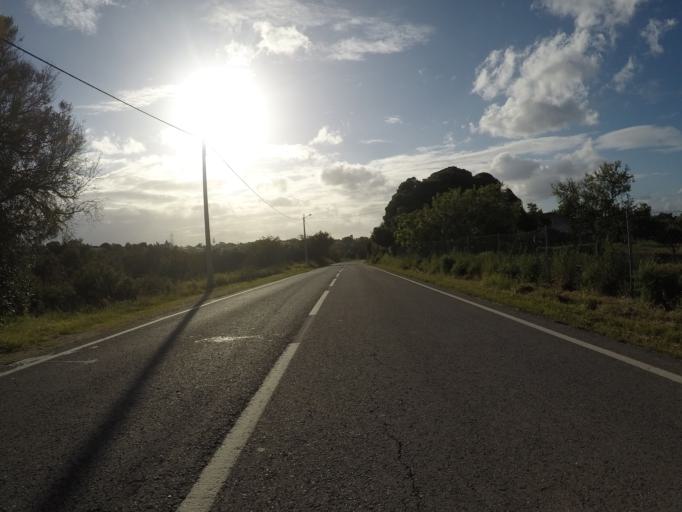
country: PT
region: Faro
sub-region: Lagoa
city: Carvoeiro
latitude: 37.1118
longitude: -8.4491
